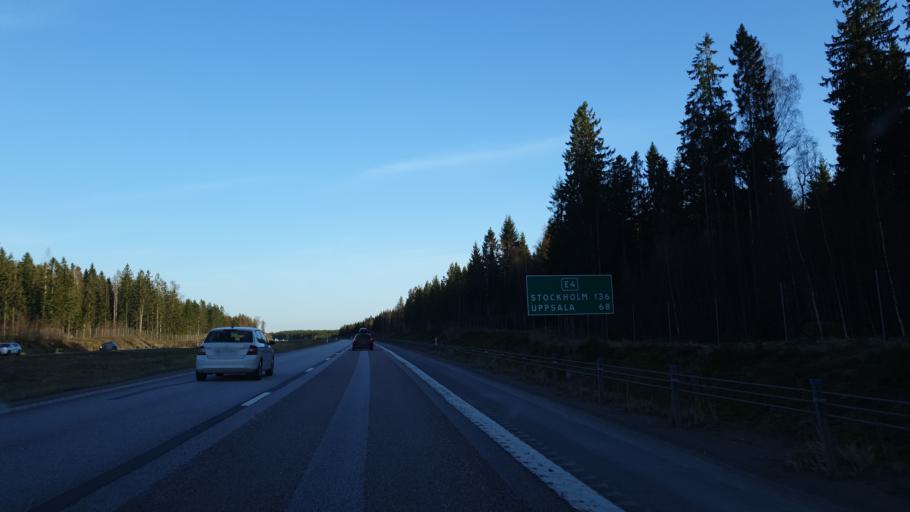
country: SE
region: Uppsala
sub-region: Tierps Kommun
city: Tierp
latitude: 60.4295
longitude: 17.4295
